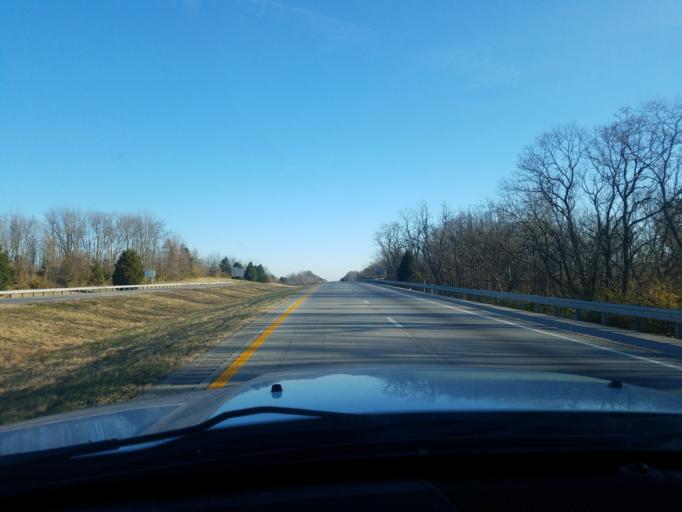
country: US
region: Kentucky
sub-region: Trimble County
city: Providence
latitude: 38.5258
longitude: -85.2302
